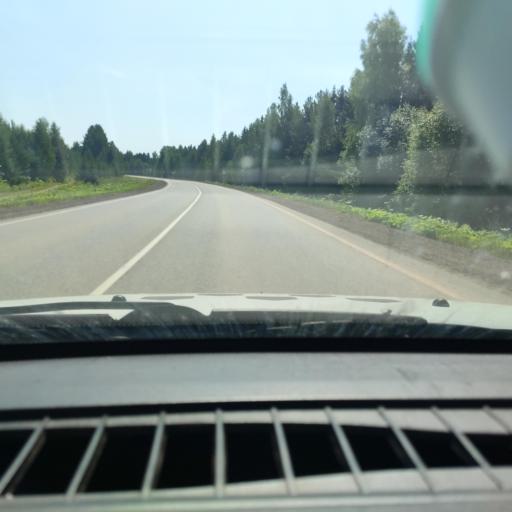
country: RU
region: Perm
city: Okhansk
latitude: 57.7090
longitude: 55.2371
